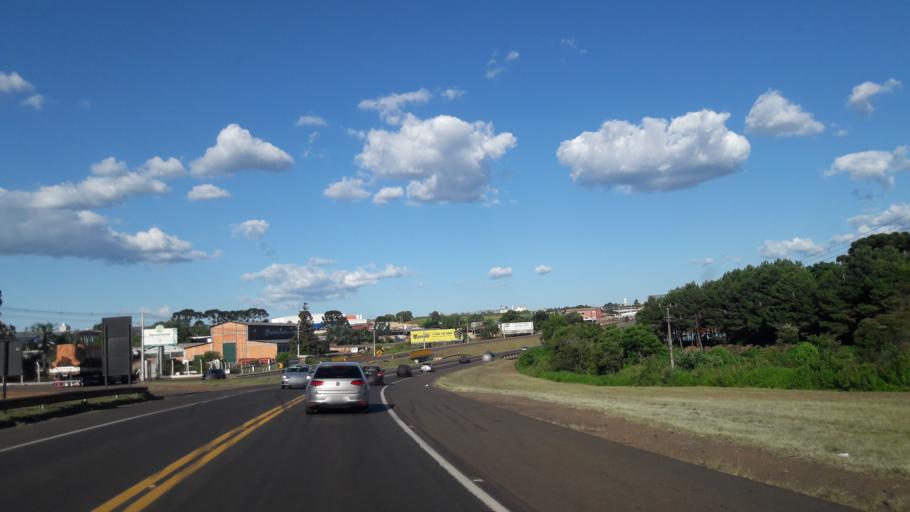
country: BR
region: Parana
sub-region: Guarapuava
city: Guarapuava
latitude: -25.3667
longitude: -51.4925
